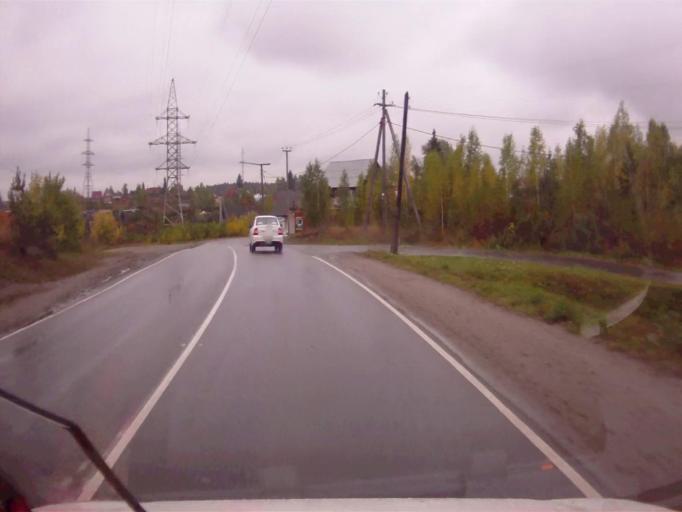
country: RU
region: Chelyabinsk
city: Kyshtym
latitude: 55.7247
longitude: 60.5202
